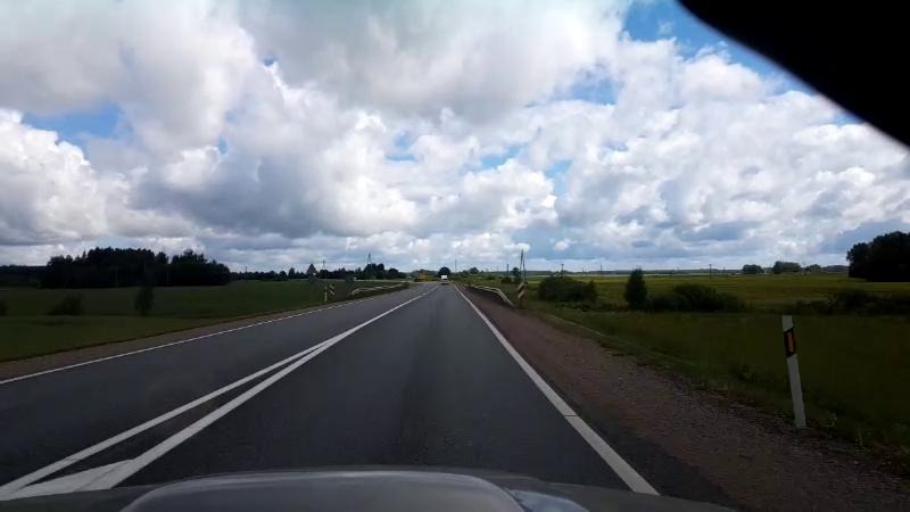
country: LV
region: Bauskas Rajons
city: Bauska
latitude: 56.4806
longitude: 24.1752
